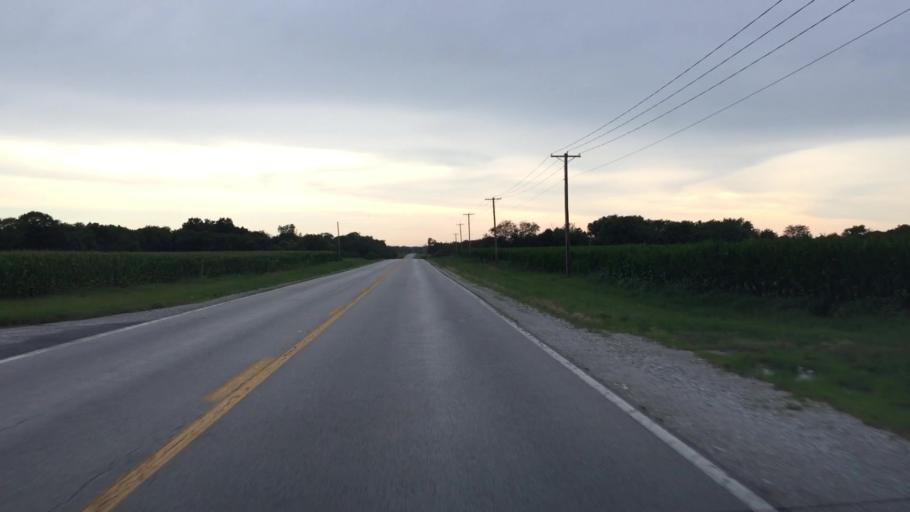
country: US
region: Illinois
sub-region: Hancock County
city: Hamilton
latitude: 40.3623
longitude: -91.3517
